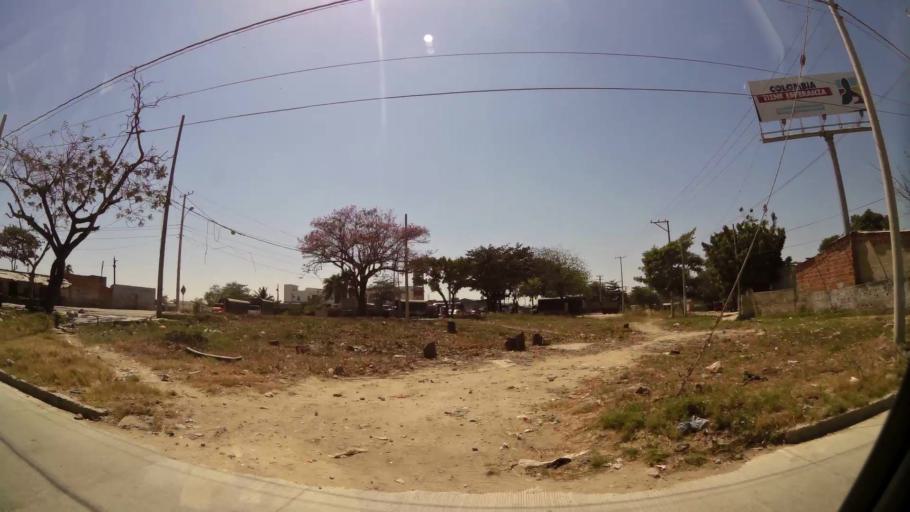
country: CO
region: Atlantico
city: Barranquilla
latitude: 10.9507
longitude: -74.7679
